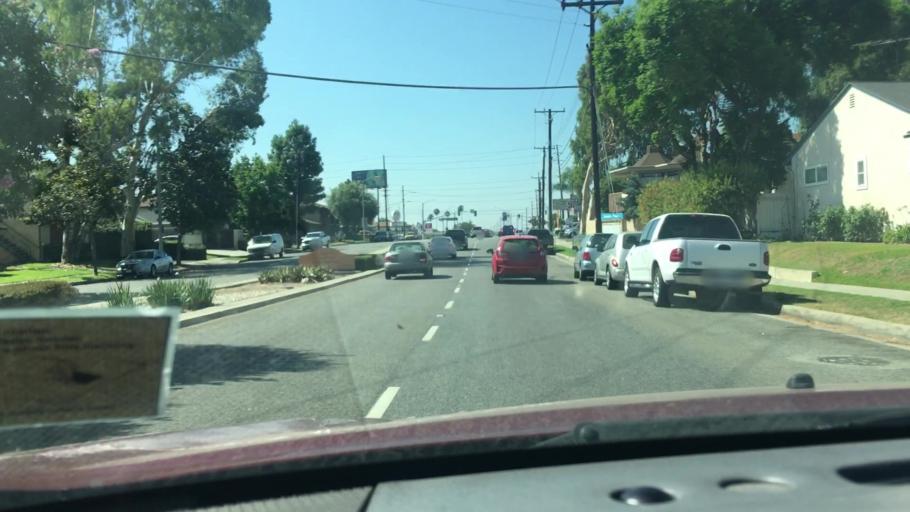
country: US
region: California
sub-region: Los Angeles County
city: La Mirada
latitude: 33.9289
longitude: -118.0119
